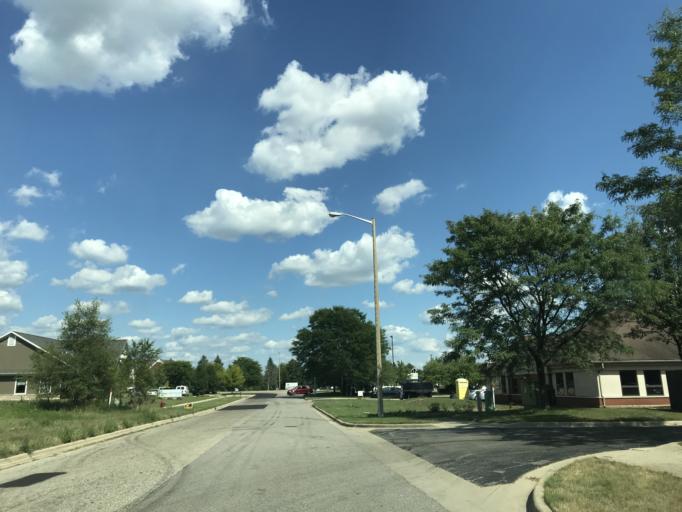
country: US
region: Michigan
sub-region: Kent County
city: Grandville
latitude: 42.8837
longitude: -85.7514
